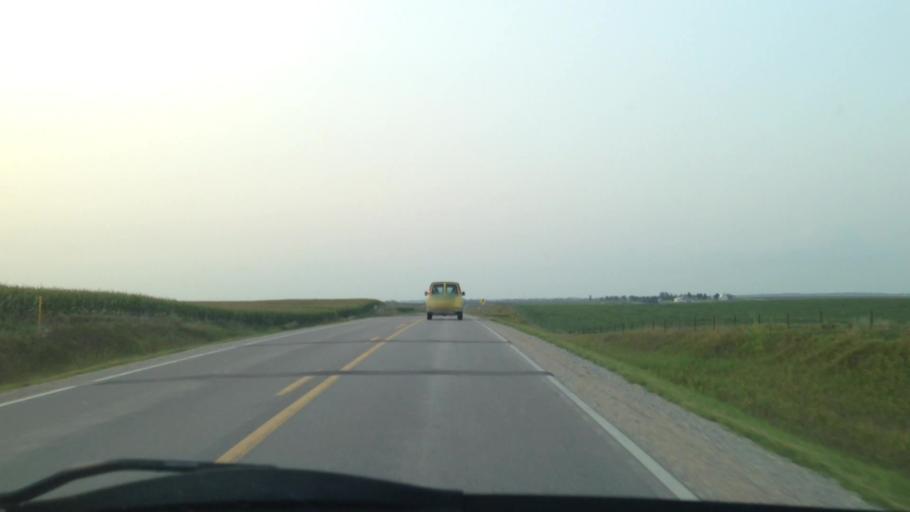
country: US
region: Iowa
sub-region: Benton County
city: Atkins
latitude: 42.0308
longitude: -91.8741
